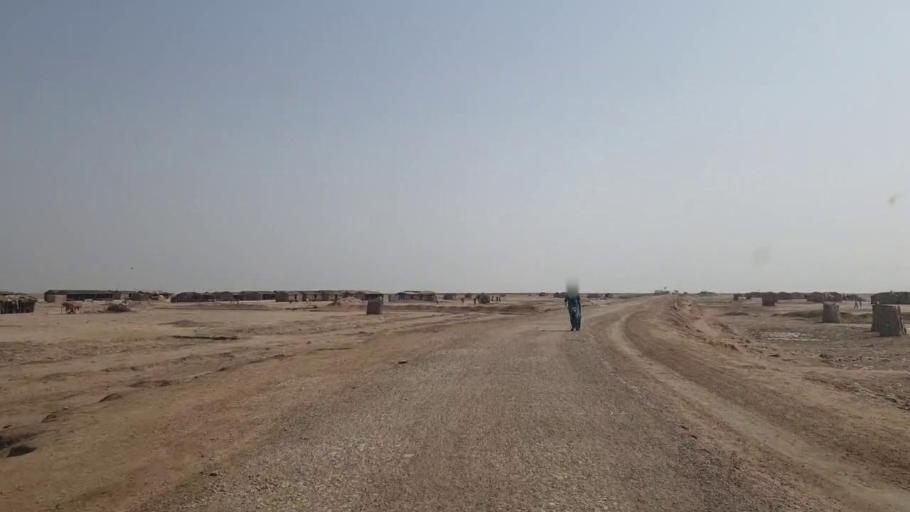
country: PK
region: Sindh
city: Jati
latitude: 24.3372
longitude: 68.5981
